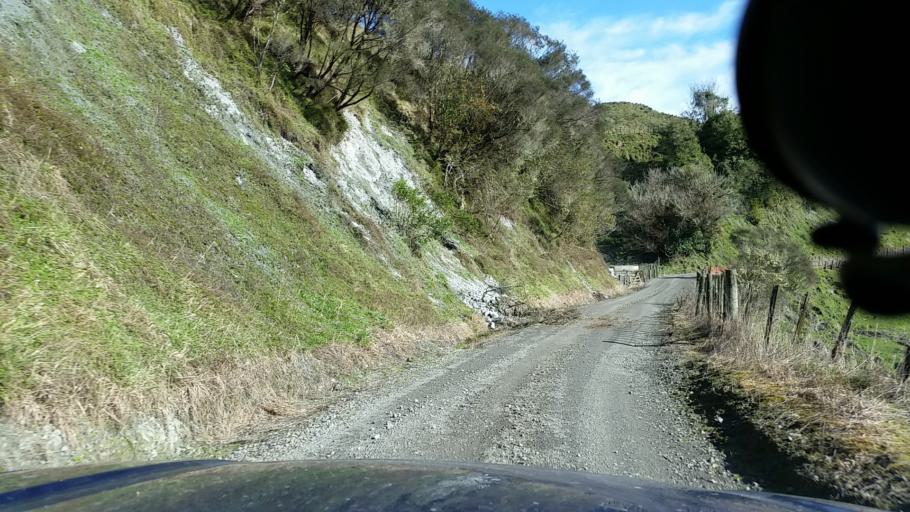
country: NZ
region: Taranaki
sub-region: New Plymouth District
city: Waitara
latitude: -39.0529
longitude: 174.7538
